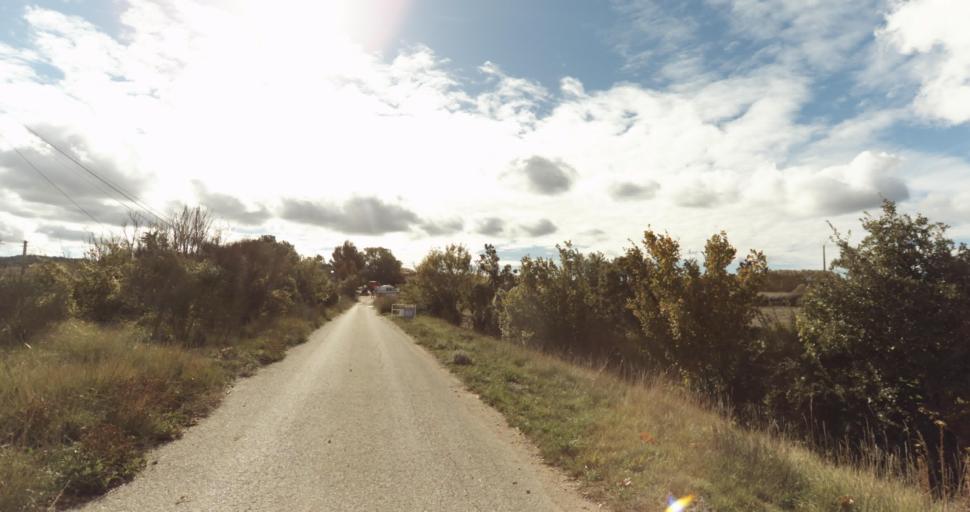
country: FR
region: Provence-Alpes-Cote d'Azur
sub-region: Departement des Bouches-du-Rhone
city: Venelles
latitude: 43.5852
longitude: 5.4846
